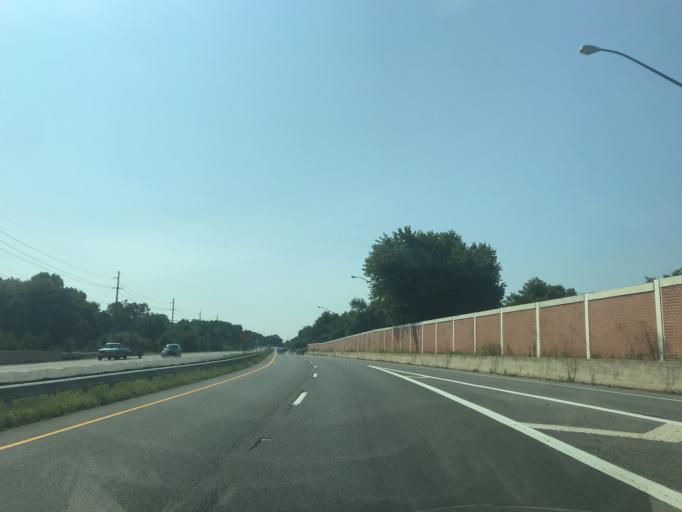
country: US
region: Maryland
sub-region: Charles County
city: Hughesville
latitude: 38.5242
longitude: -76.7793
